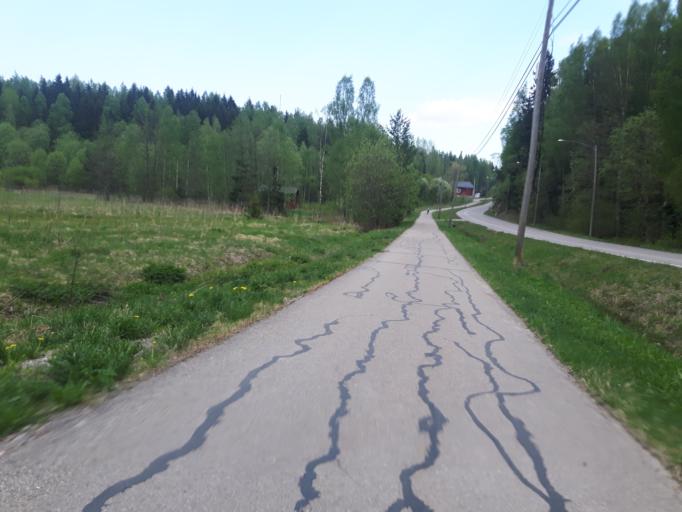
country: FI
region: Uusimaa
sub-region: Porvoo
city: Porvoo
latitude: 60.3997
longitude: 25.7280
